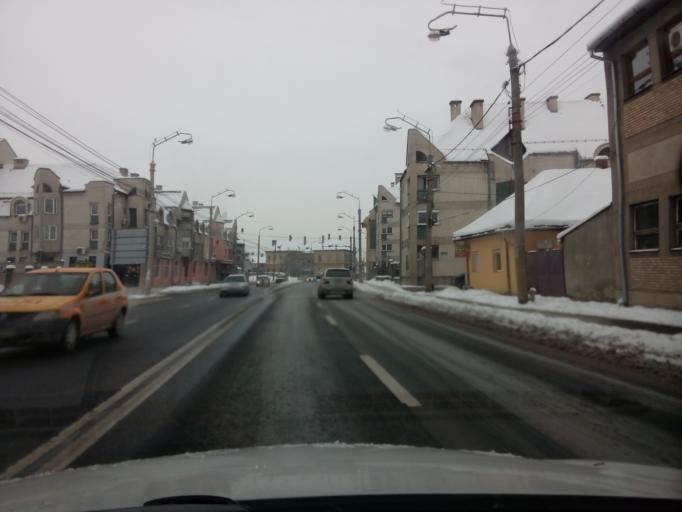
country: RO
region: Sibiu
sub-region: Municipiul Sibiu
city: Sibiu
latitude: 45.7979
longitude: 24.1581
